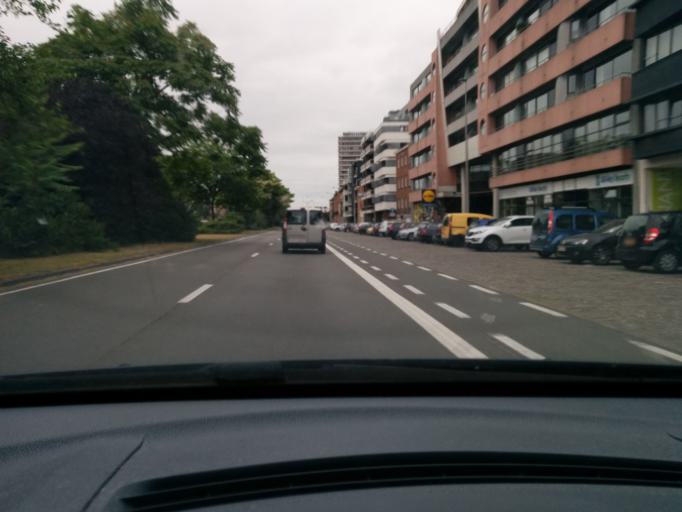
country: BE
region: Flanders
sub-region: Provincie Oost-Vlaanderen
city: Gent
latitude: 51.0508
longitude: 3.7021
